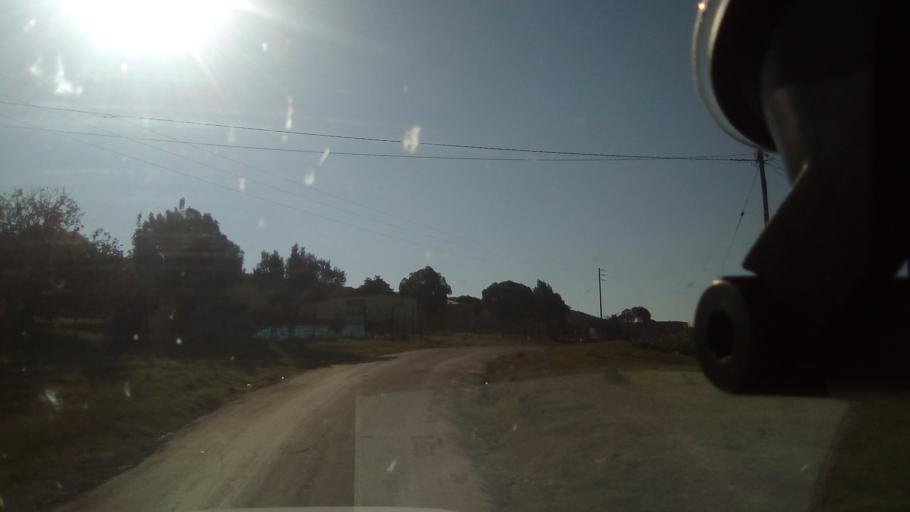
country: ZA
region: Eastern Cape
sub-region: Buffalo City Metropolitan Municipality
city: Bhisho
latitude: -32.8148
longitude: 27.3530
